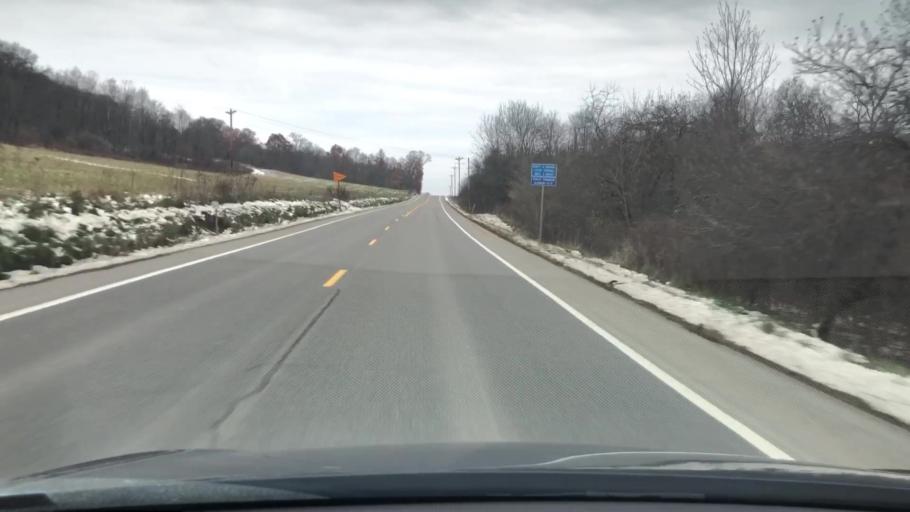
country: US
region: Pennsylvania
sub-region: Jefferson County
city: Brookville
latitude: 41.0659
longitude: -79.2417
